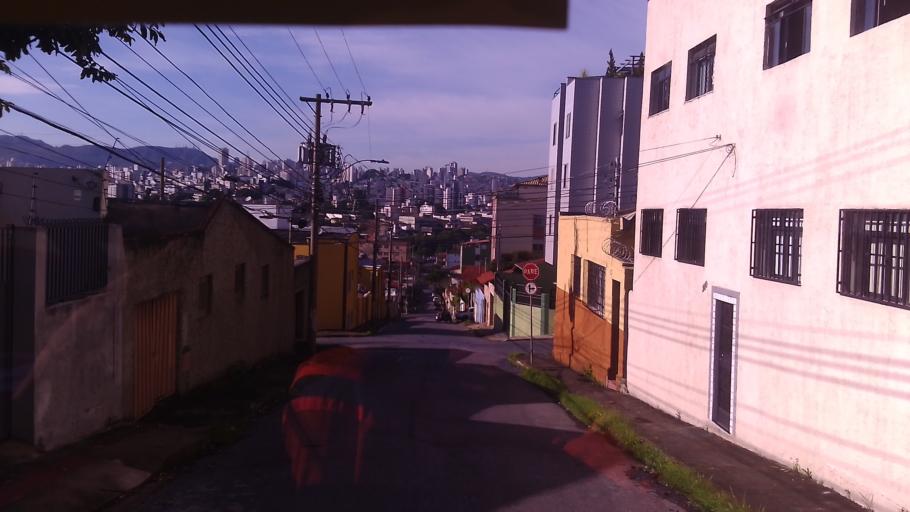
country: BR
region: Minas Gerais
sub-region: Belo Horizonte
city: Belo Horizonte
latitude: -19.9166
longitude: -43.9724
